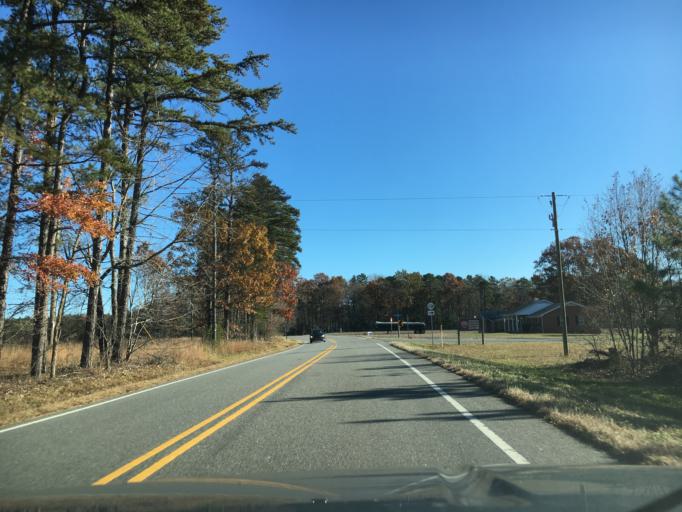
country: US
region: Virginia
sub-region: Buckingham County
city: Buckingham
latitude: 37.4580
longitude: -78.6811
